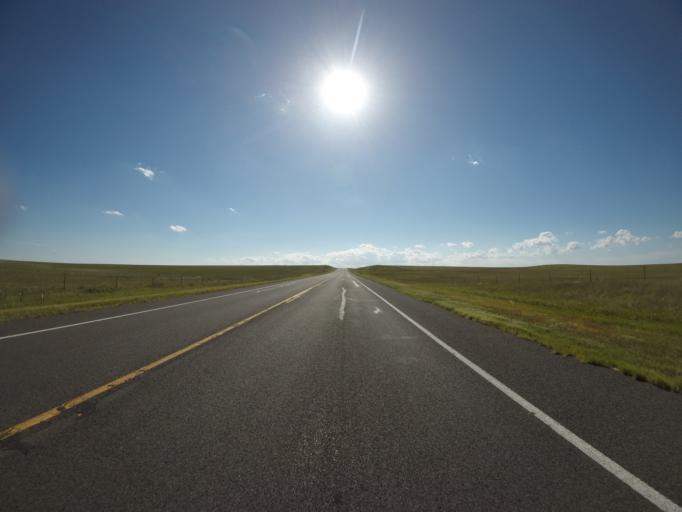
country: US
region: Colorado
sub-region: Logan County
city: Sterling
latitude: 40.6110
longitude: -103.5629
